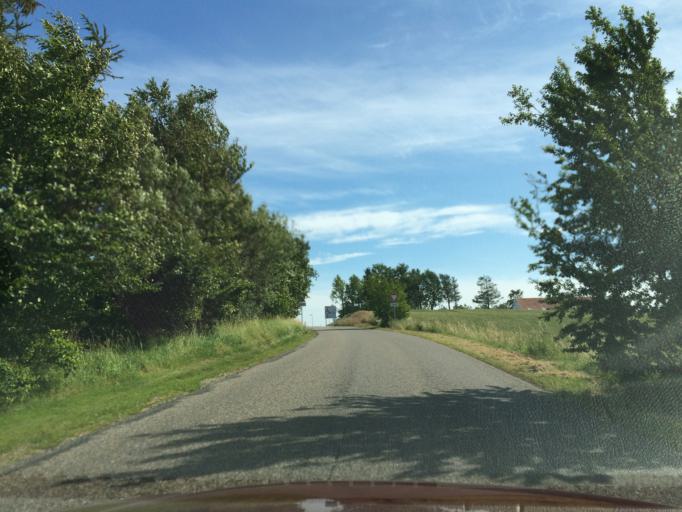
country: DK
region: Central Jutland
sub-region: Silkeborg Kommune
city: Silkeborg
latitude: 56.2105
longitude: 9.5619
